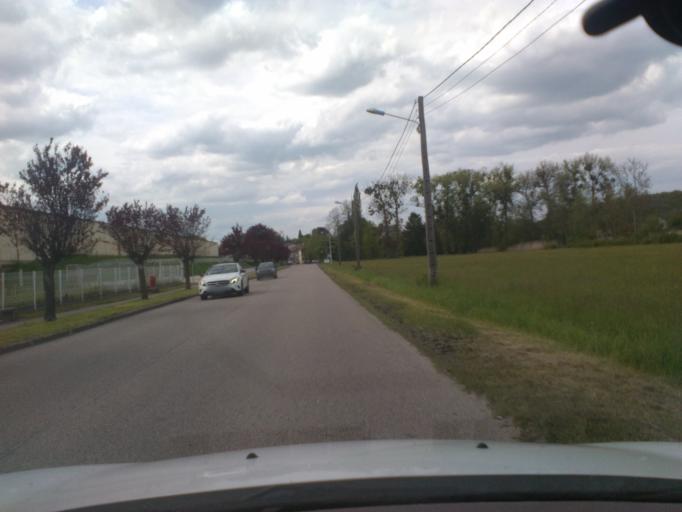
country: FR
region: Lorraine
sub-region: Departement des Vosges
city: Mirecourt
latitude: 48.2752
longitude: 6.1358
